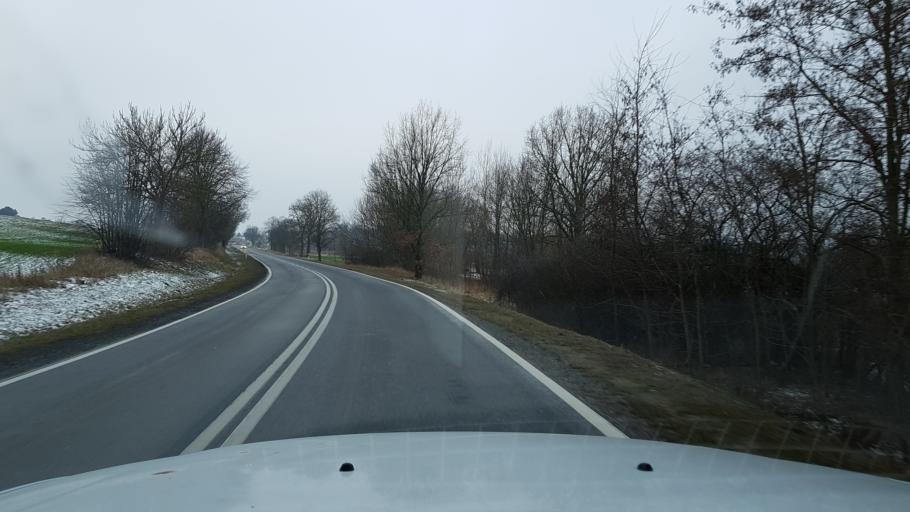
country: PL
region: West Pomeranian Voivodeship
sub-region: Powiat gryfinski
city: Widuchowa
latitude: 53.1581
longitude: 14.4402
